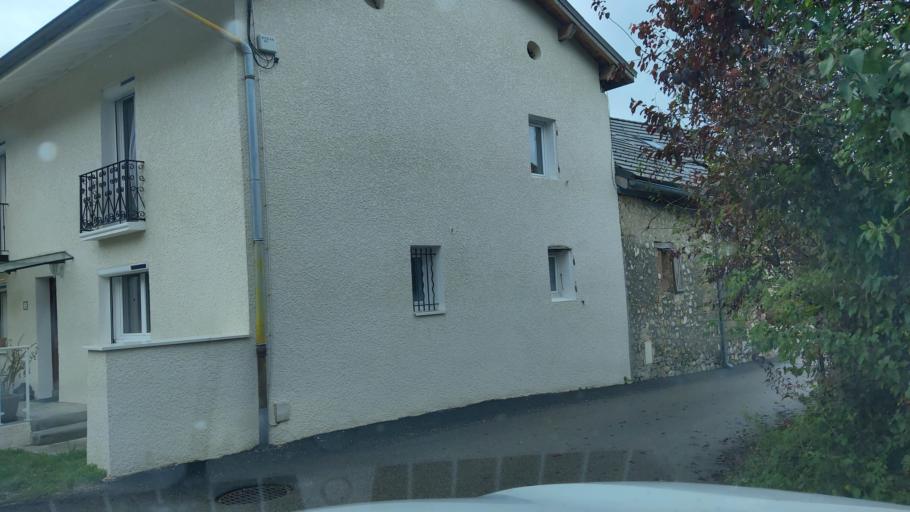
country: FR
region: Rhone-Alpes
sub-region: Departement de la Savoie
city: Les Marches
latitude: 45.5076
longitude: 5.9998
